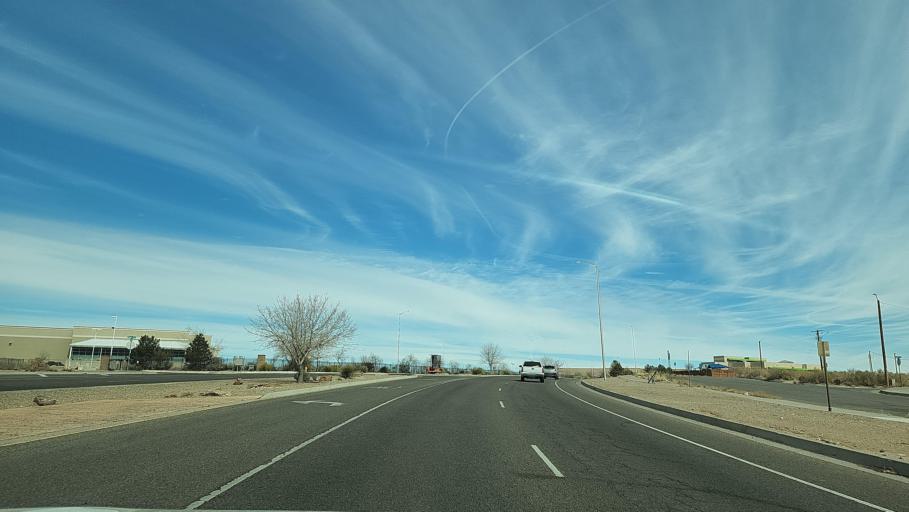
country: US
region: New Mexico
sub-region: Bernalillo County
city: Albuquerque
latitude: 35.0754
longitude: -106.7134
